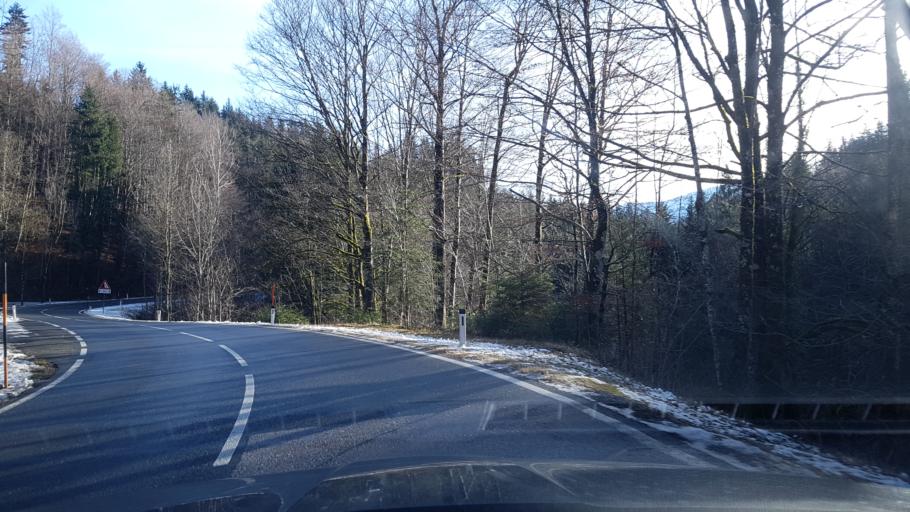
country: AT
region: Salzburg
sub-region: Politischer Bezirk Hallein
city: Krispl
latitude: 47.7232
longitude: 13.1879
